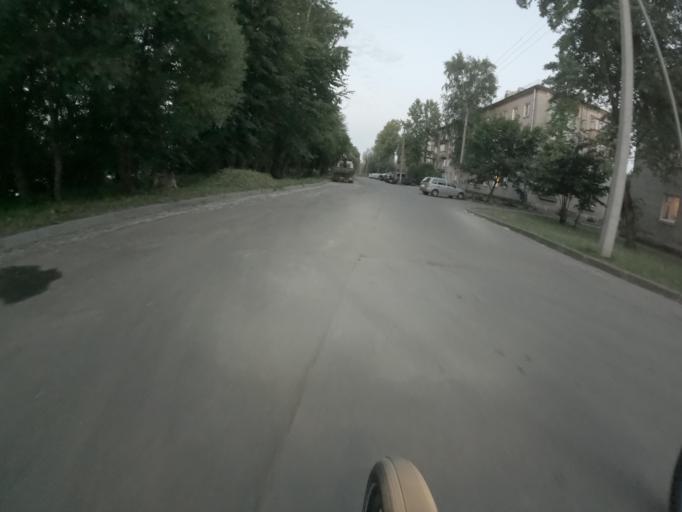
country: RU
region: St.-Petersburg
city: Sapernyy
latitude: 59.7794
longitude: 30.6931
